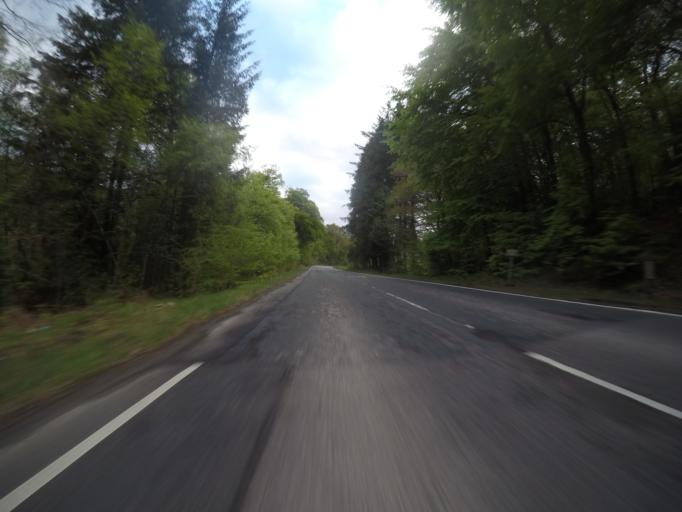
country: GB
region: Scotland
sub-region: Highland
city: Spean Bridge
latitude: 57.0808
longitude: -4.7612
